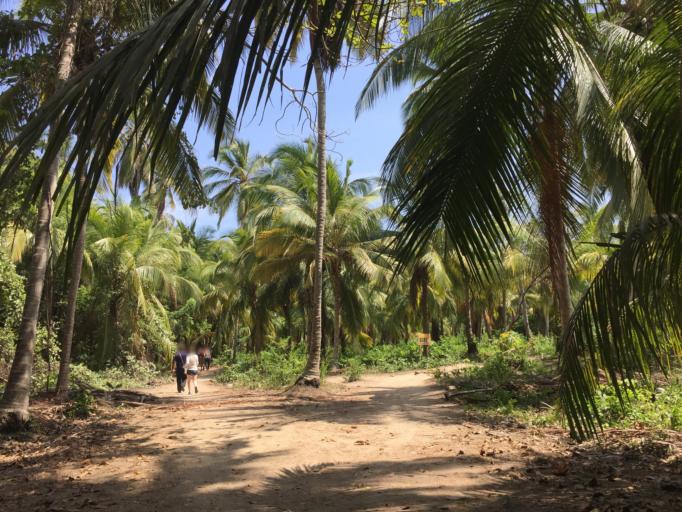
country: CO
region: Magdalena
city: Santa Marta
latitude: 11.3160
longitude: -73.9533
